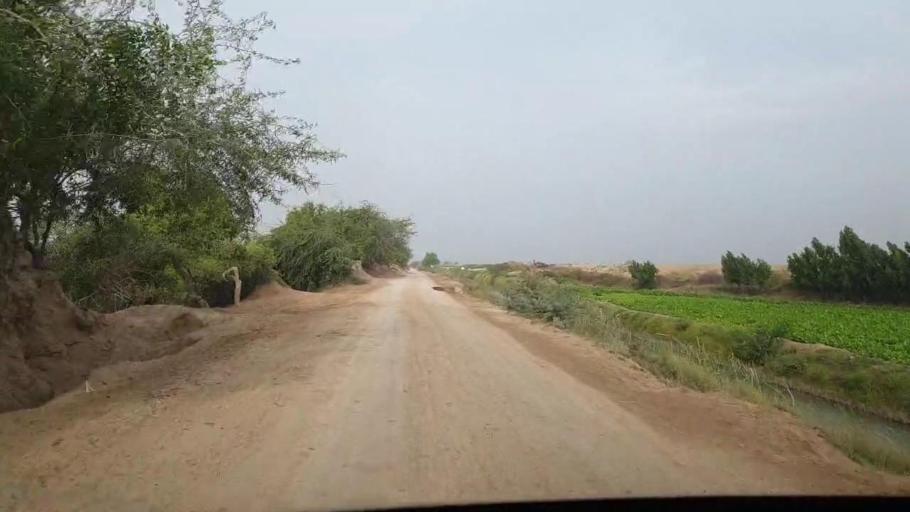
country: PK
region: Sindh
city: Chuhar Jamali
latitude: 24.3979
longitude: 67.9705
